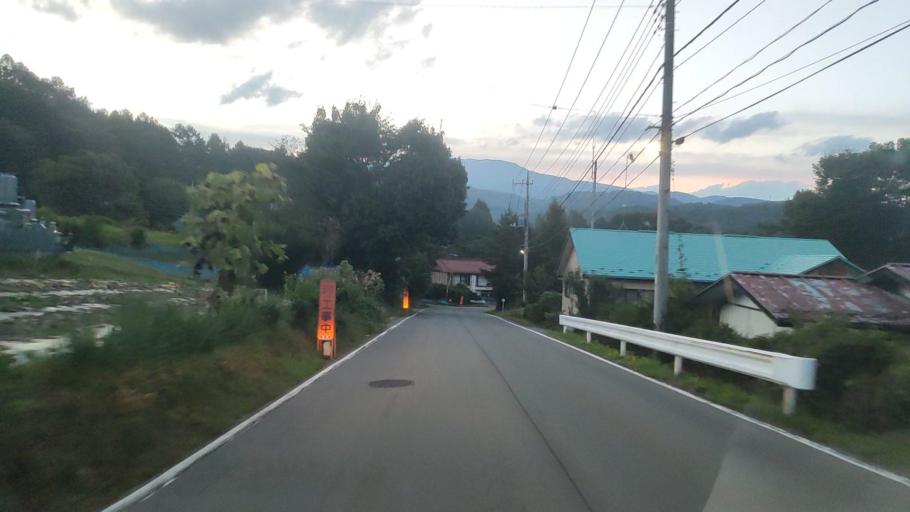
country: JP
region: Gunma
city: Nakanojomachi
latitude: 36.5423
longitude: 138.6027
